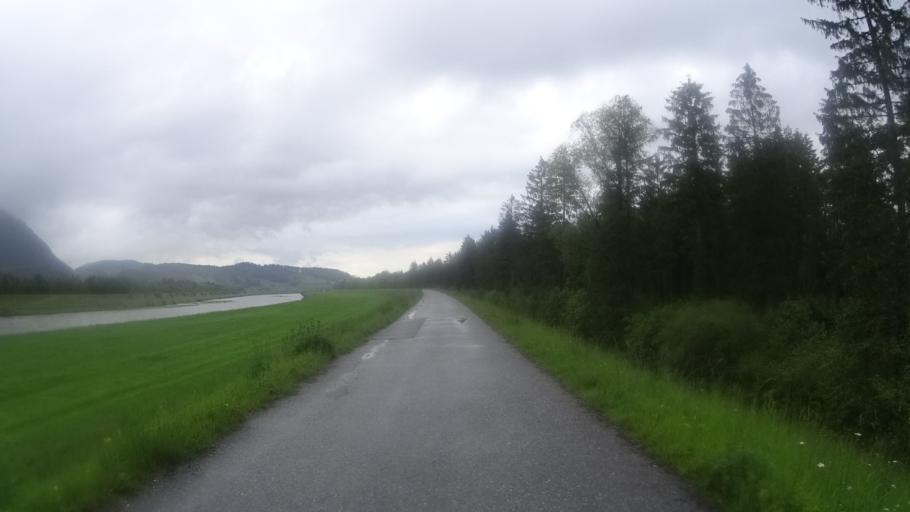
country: CH
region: Saint Gallen
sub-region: Wahlkreis Rheintal
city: Ruthi
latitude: 47.2843
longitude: 9.5515
